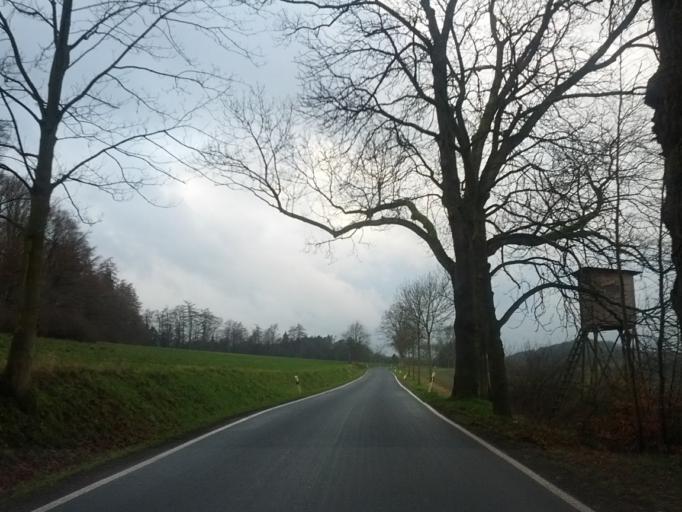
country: DE
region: Thuringia
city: Wolfsburg-Unkeroda
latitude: 50.9223
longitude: 10.2862
